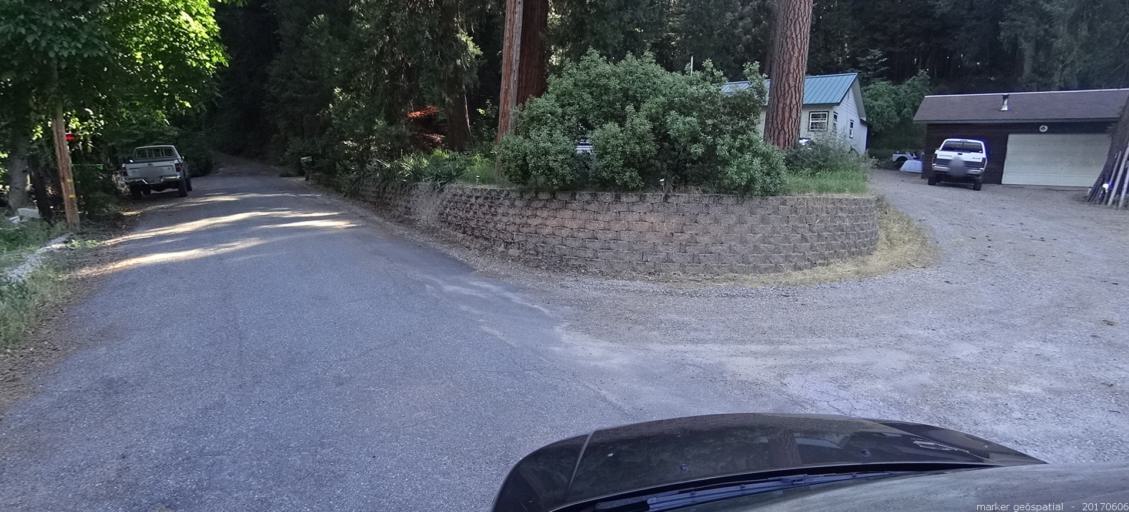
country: US
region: California
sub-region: Siskiyou County
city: Dunsmuir
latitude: 41.2001
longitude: -122.2712
